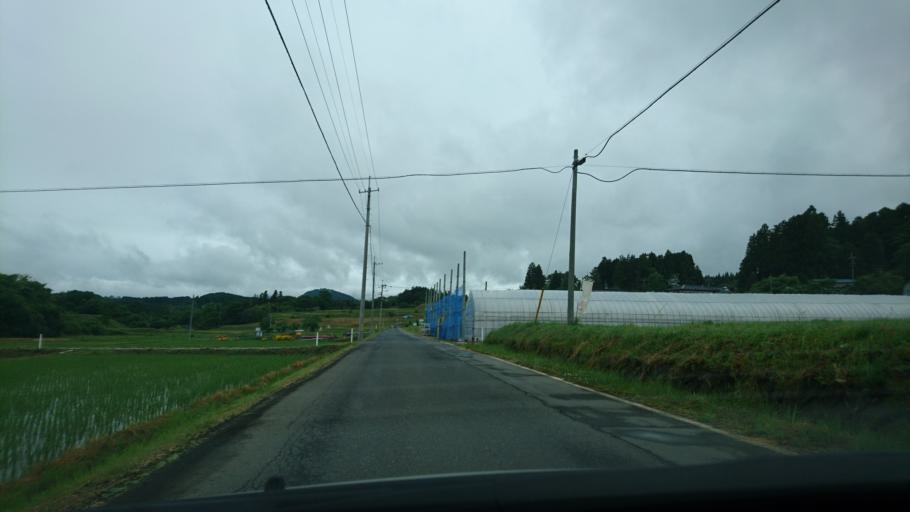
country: JP
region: Iwate
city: Ichinoseki
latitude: 38.9234
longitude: 141.2093
